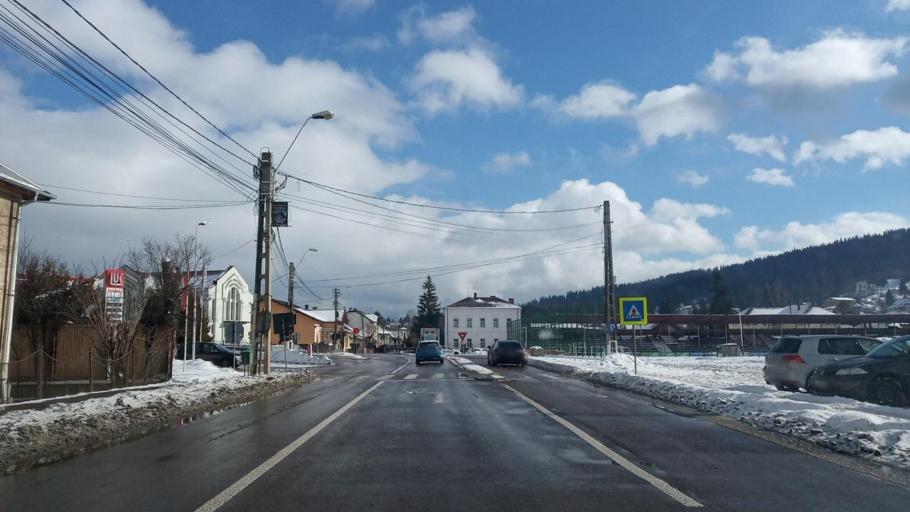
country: RO
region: Suceava
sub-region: Municipiul Vatra Dornei
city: Vatra Dornei
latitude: 47.3461
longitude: 25.3463
